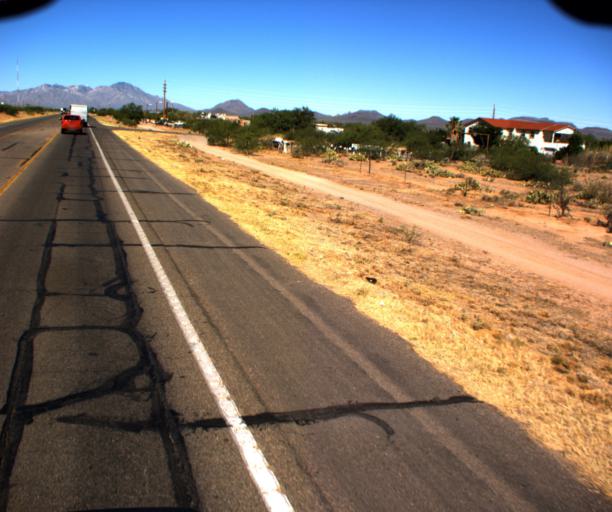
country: US
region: Arizona
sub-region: Pima County
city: Three Points
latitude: 32.0860
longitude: -111.2902
